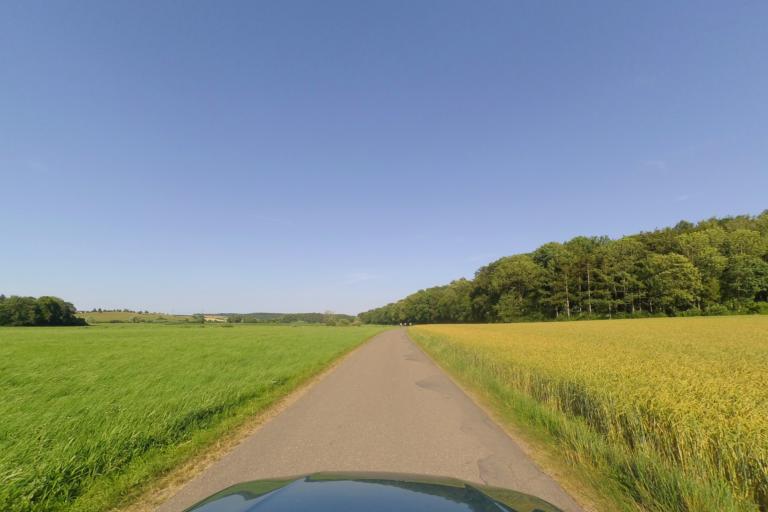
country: DE
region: Baden-Wuerttemberg
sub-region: Regierungsbezirk Stuttgart
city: Hermaringen
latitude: 48.5811
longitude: 10.2461
